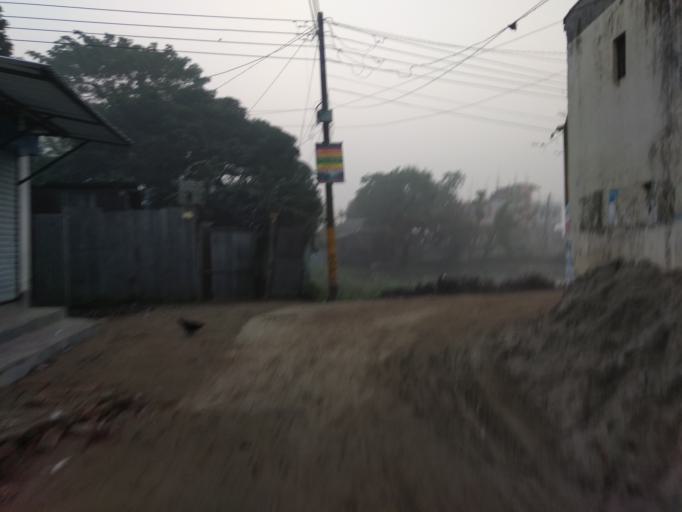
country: BD
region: Dhaka
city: Tungi
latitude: 23.8565
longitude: 90.4367
